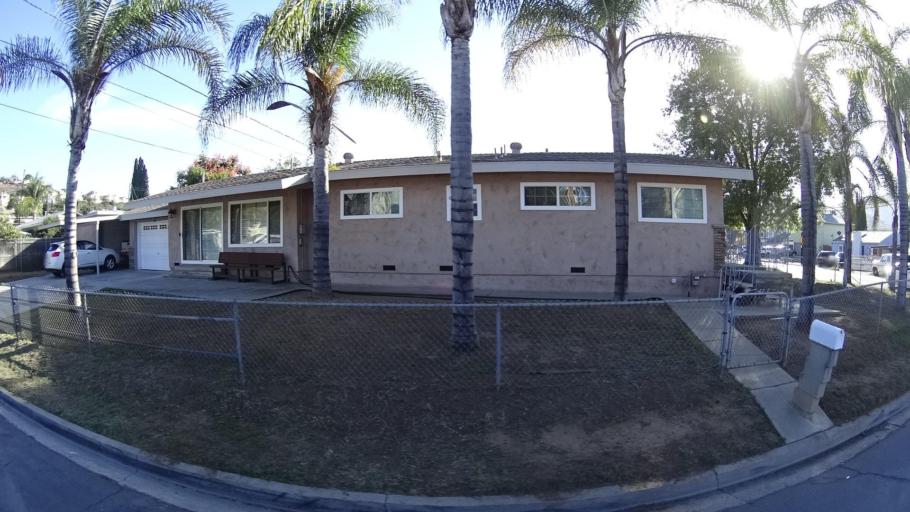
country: US
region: California
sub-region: San Diego County
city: La Presa
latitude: 32.7087
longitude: -116.9881
